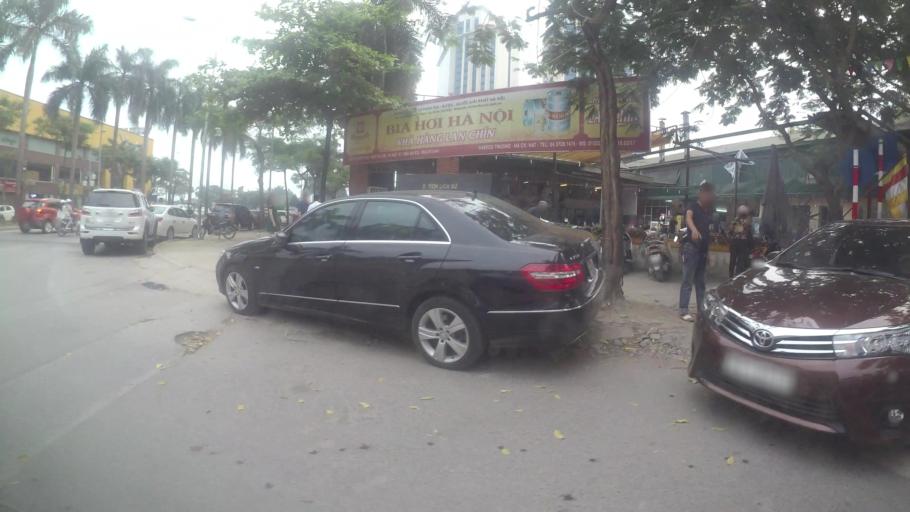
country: VN
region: Ha Noi
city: Cau Dien
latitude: 21.0290
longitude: 105.7684
